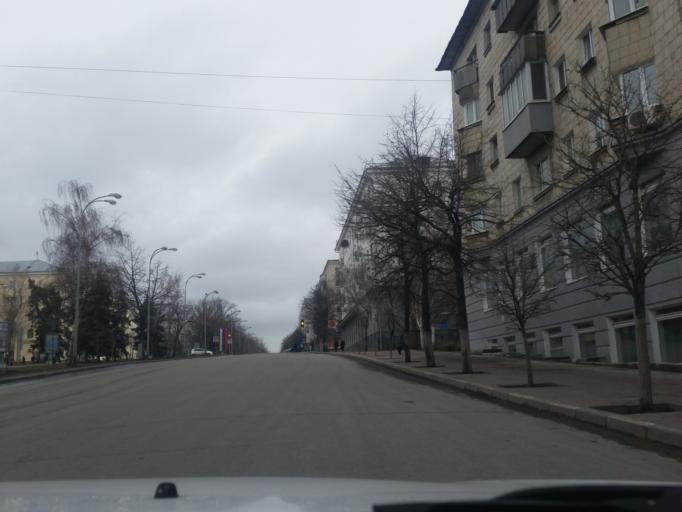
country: RU
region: Ulyanovsk
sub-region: Ulyanovskiy Rayon
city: Ulyanovsk
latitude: 54.3088
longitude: 48.3967
